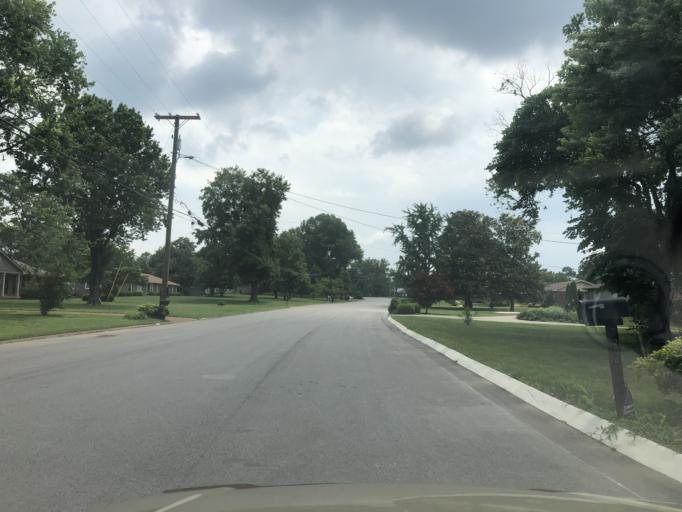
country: US
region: Tennessee
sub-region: Davidson County
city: Lakewood
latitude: 36.2359
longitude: -86.6210
